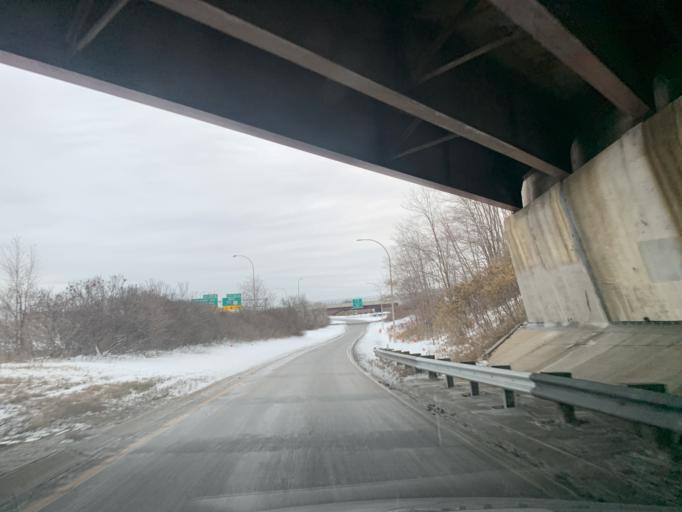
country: US
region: Minnesota
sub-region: Hennepin County
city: Minneapolis
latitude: 44.9920
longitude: -93.2860
